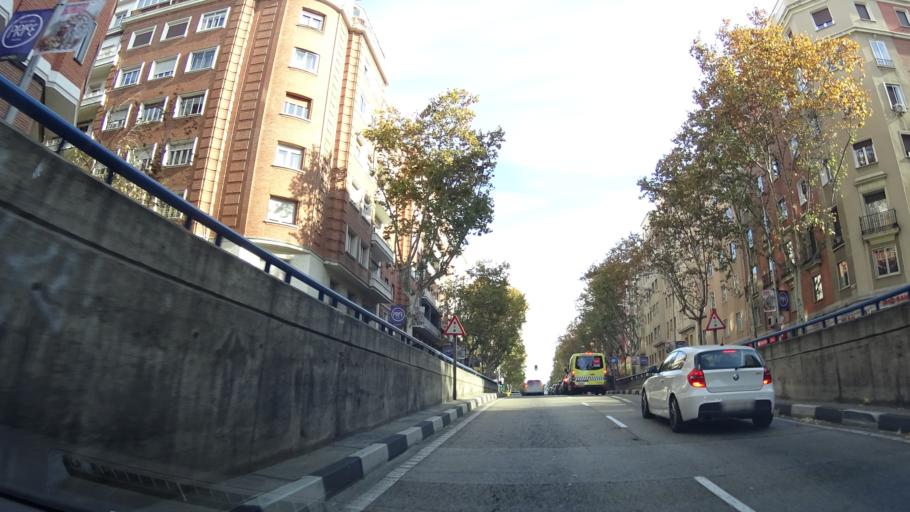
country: ES
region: Madrid
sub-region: Provincia de Madrid
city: Chamberi
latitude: 40.4390
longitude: -3.7112
